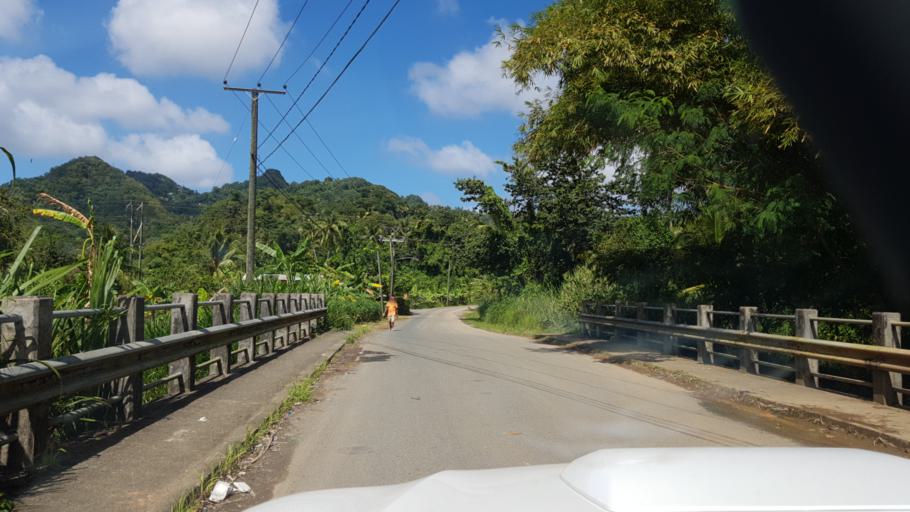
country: LC
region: Castries Quarter
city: Castries
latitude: 13.9764
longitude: -60.9774
